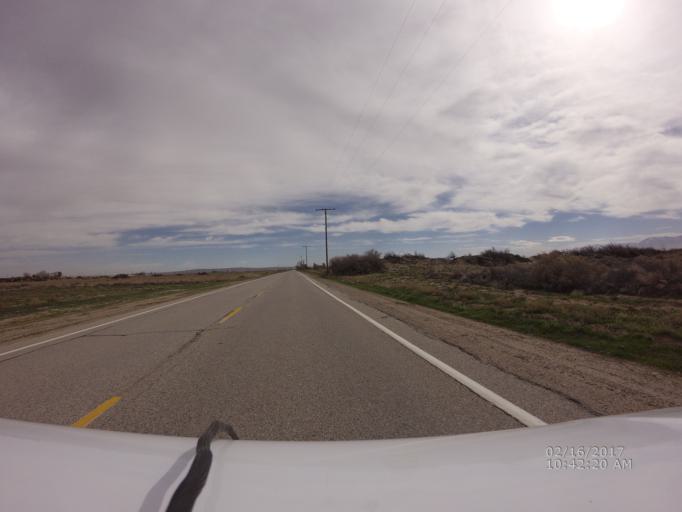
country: US
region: California
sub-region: Los Angeles County
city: Lancaster
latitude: 34.7196
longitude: -117.9791
